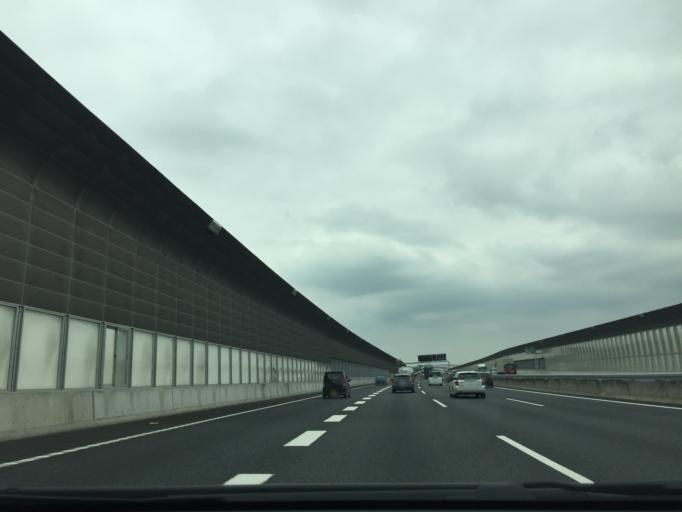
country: JP
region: Aichi
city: Obu
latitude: 35.0451
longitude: 136.9542
